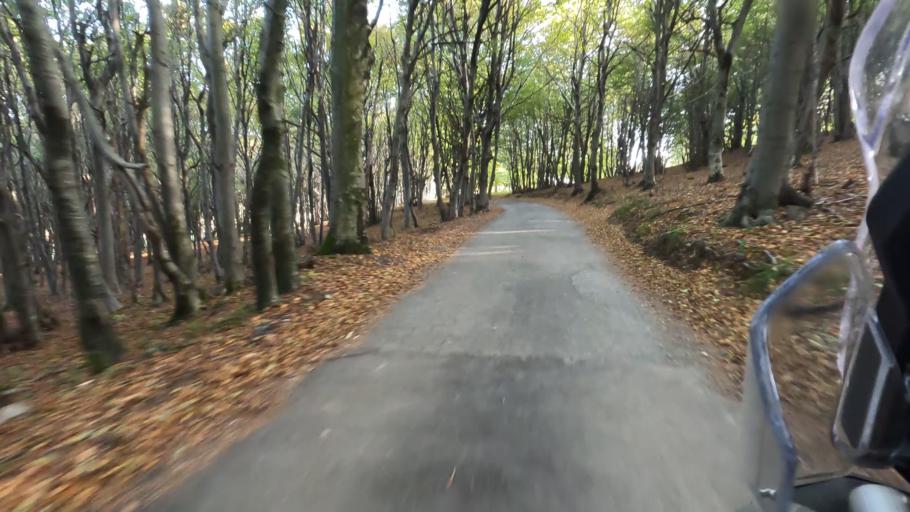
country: IT
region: Liguria
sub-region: Provincia di Genova
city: Sciarborasca
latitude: 44.4298
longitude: 8.5868
